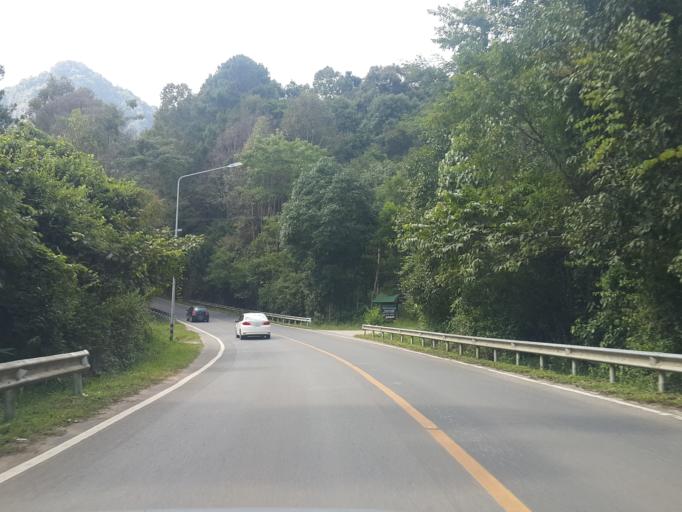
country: TH
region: Chiang Mai
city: Chom Thong
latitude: 18.5478
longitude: 98.5443
